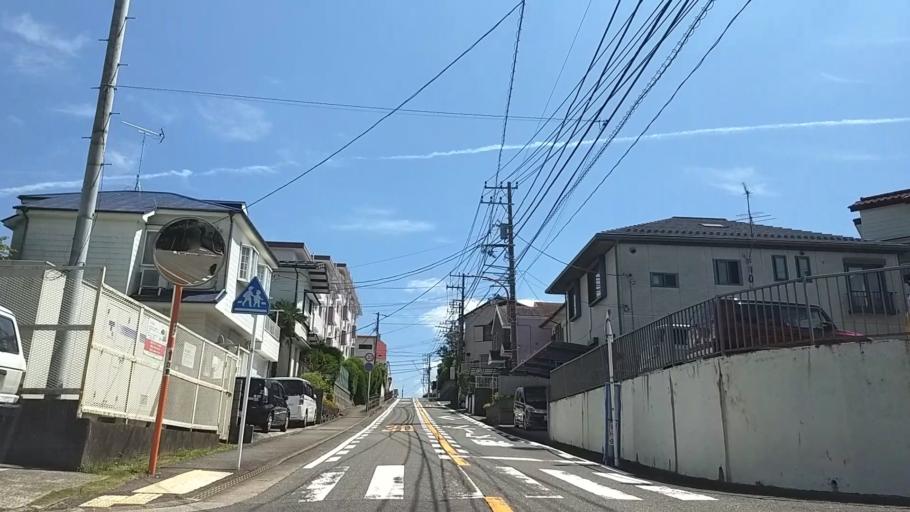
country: JP
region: Kanagawa
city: Zushi
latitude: 35.2920
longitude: 139.5911
